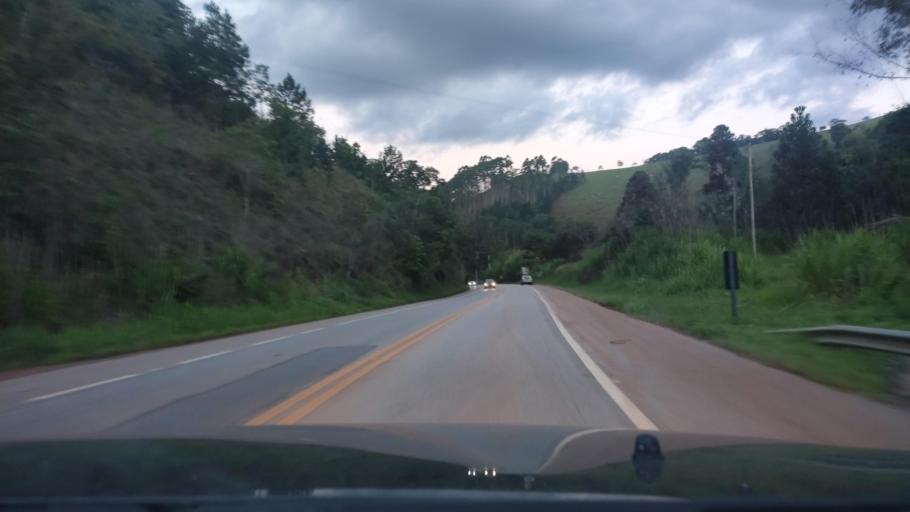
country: BR
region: Sao Paulo
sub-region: Campos Do Jordao
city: Campos do Jordao
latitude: -22.7973
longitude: -45.7493
